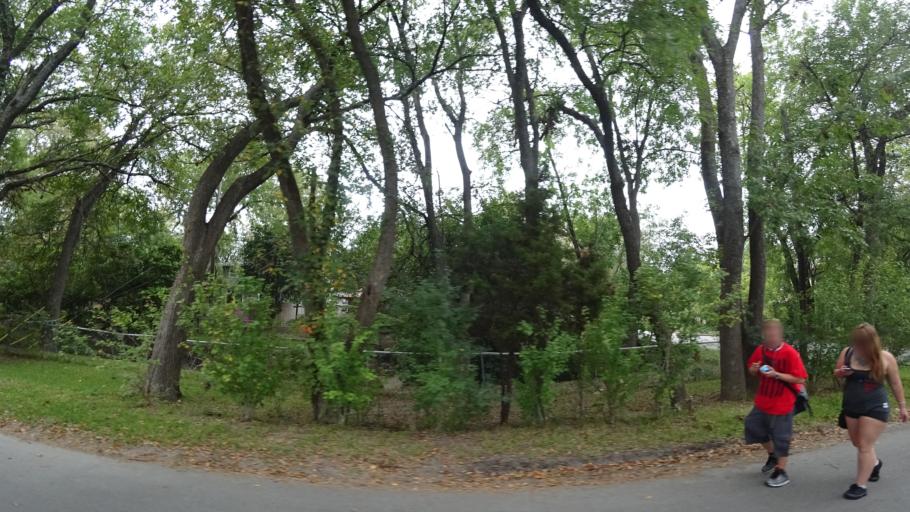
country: US
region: Texas
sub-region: Travis County
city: Austin
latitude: 30.2093
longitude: -97.7770
